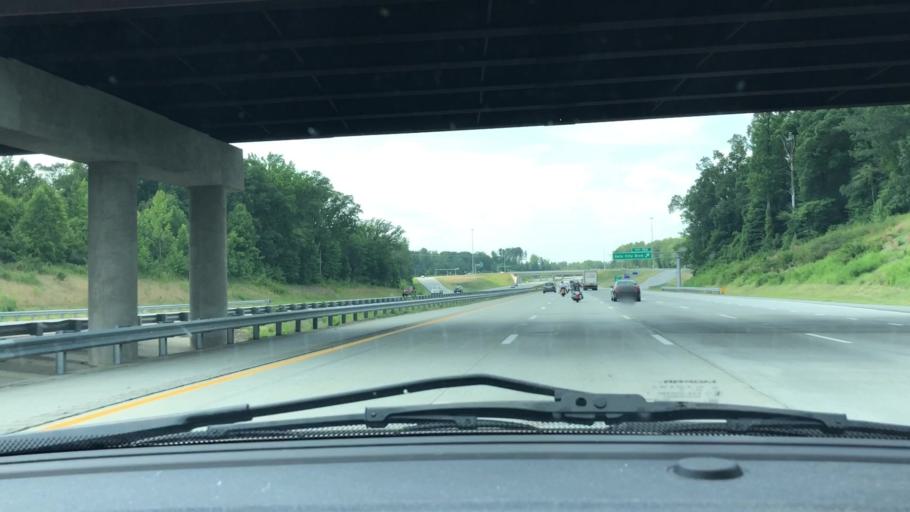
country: US
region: North Carolina
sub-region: Guilford County
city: Jamestown
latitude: 36.0225
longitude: -79.8782
